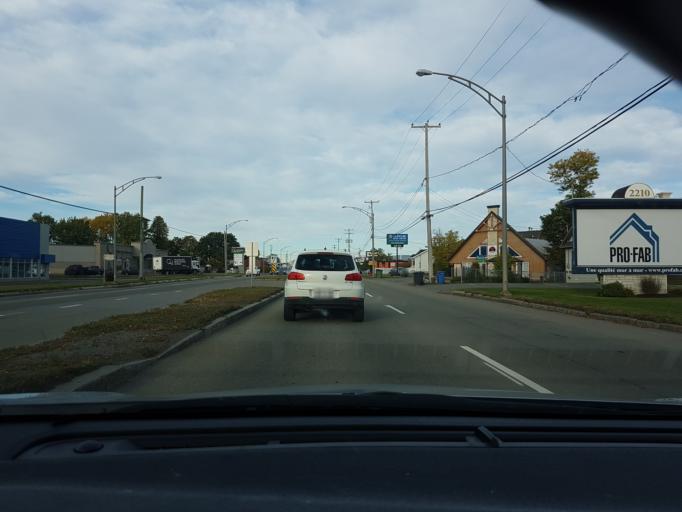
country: CA
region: Quebec
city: L'Ancienne-Lorette
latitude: 46.8066
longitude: -71.2923
